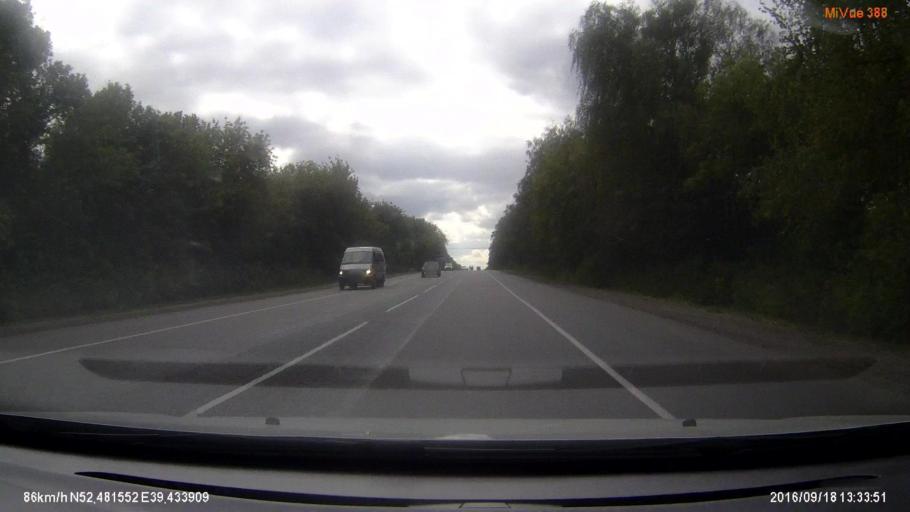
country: RU
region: Lipetsk
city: Borinskoye
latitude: 52.4818
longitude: 39.4343
